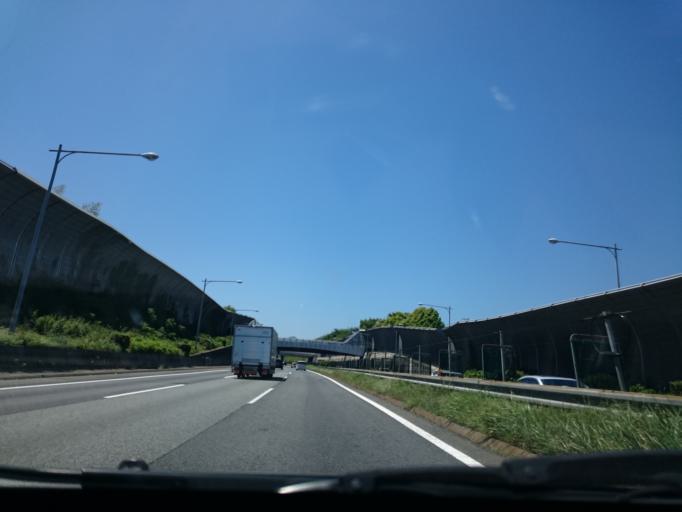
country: JP
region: Kanagawa
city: Atsugi
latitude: 35.4238
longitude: 139.3398
